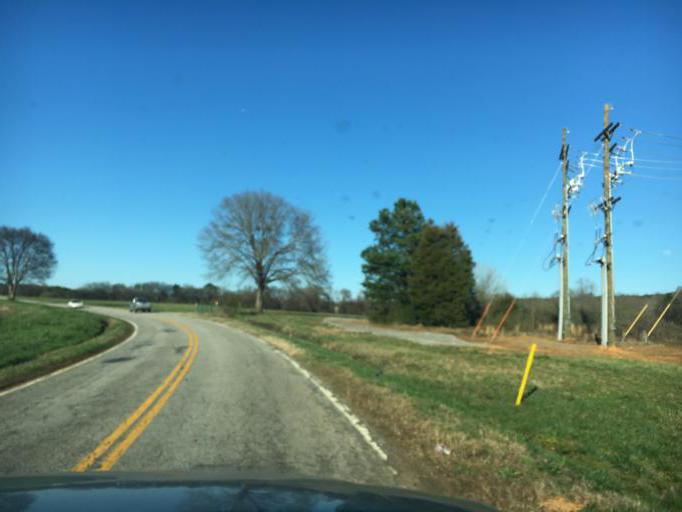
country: US
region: South Carolina
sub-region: Spartanburg County
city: Roebuck
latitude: 34.8658
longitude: -82.0256
